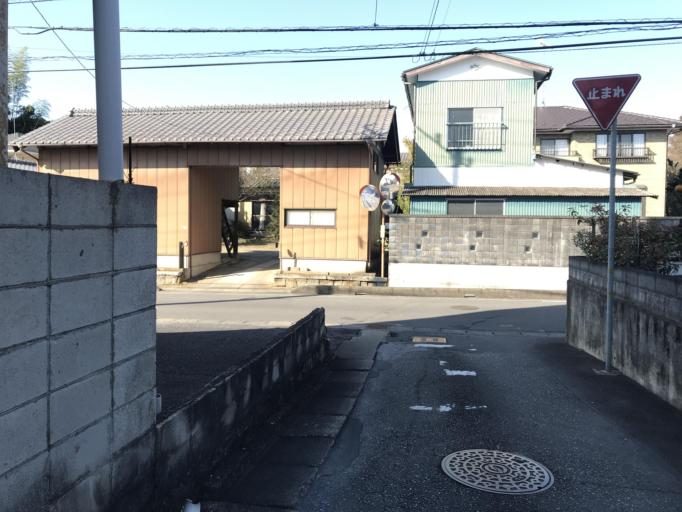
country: JP
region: Ibaraki
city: Ishioka
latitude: 36.1878
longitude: 140.2712
